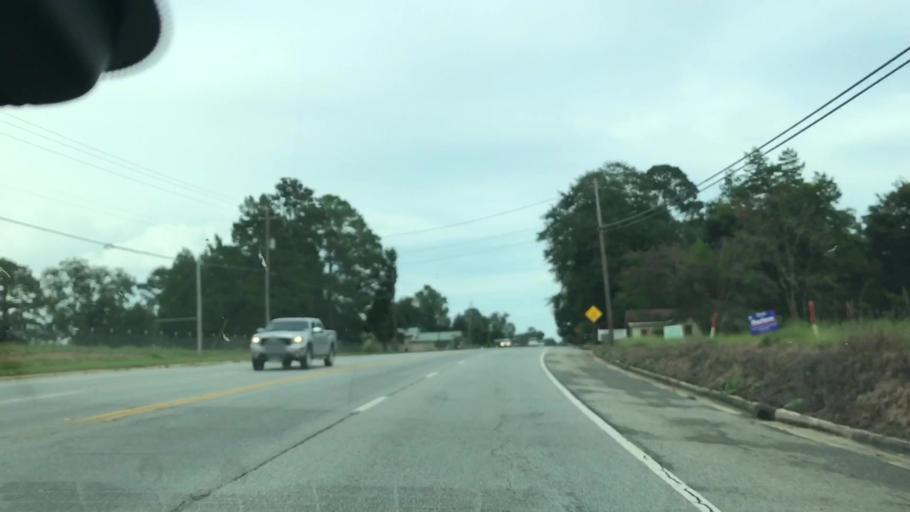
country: US
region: Georgia
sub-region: Quitman County
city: Georgetown
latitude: 31.8846
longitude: -85.1001
